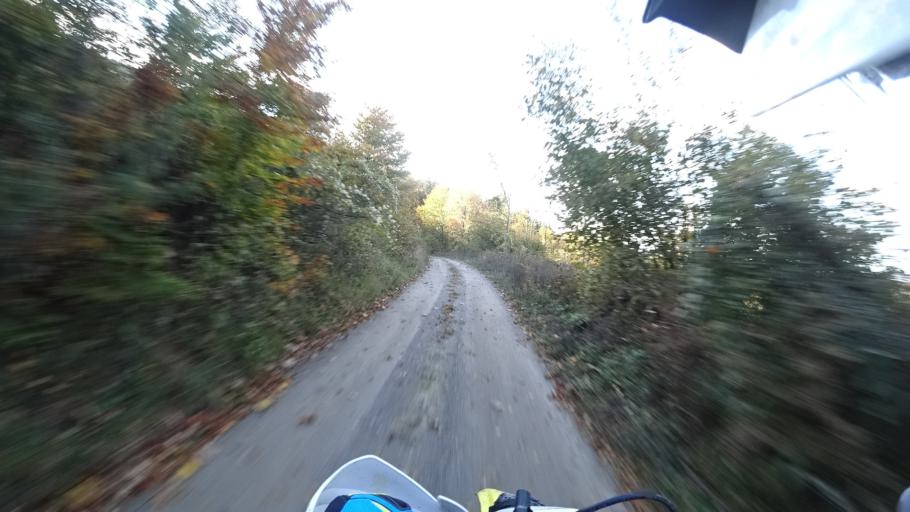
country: HR
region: Karlovacka
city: Plaski
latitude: 45.0350
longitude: 15.3776
